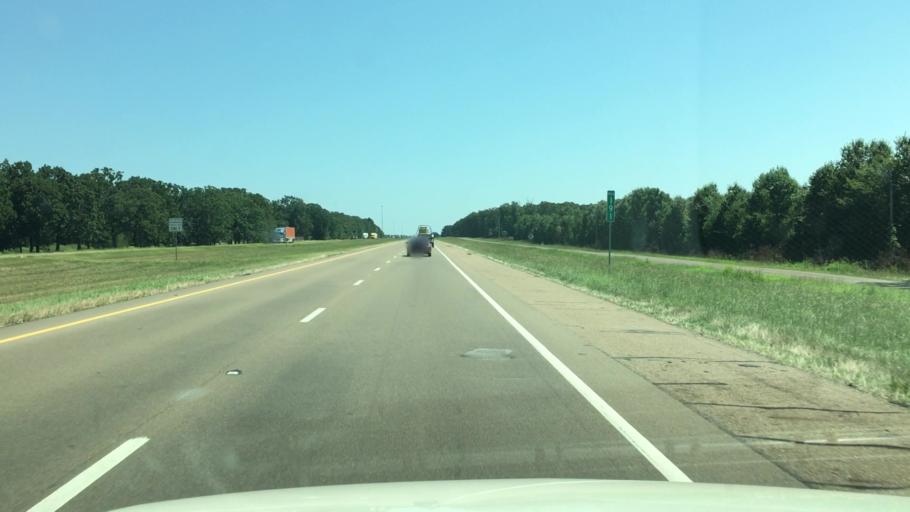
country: US
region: Texas
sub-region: Bowie County
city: De Kalb
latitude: 33.4050
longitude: -94.5717
